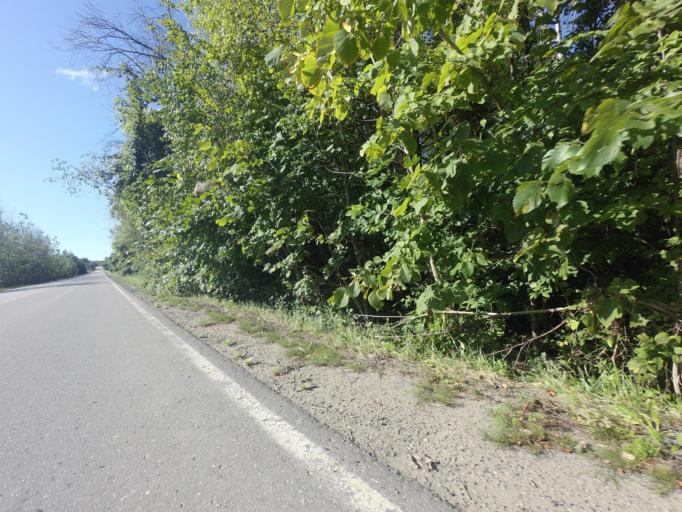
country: CA
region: Ontario
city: Bradford West Gwillimbury
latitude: 44.0494
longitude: -79.5579
